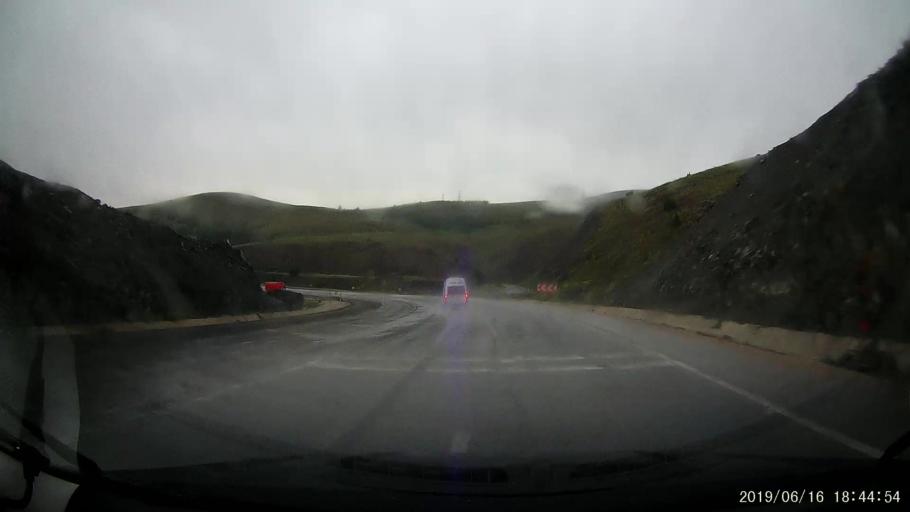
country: TR
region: Erzincan
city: Doganbeyli
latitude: 39.8711
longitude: 39.0658
